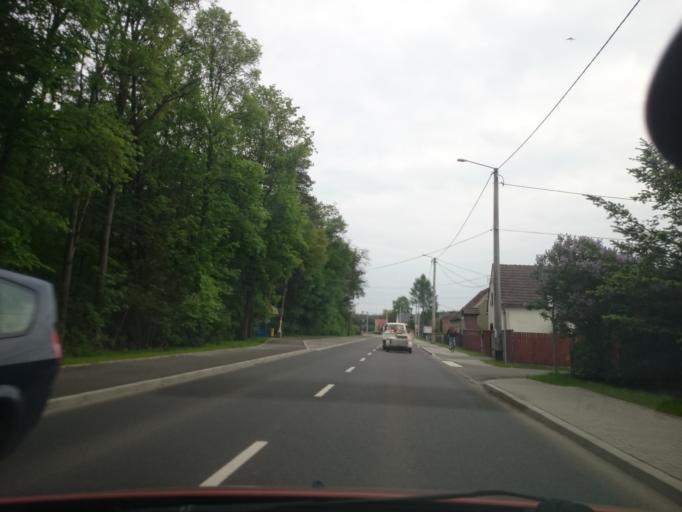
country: PL
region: Opole Voivodeship
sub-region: Powiat opolski
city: Kup
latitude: 50.8136
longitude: 17.8826
